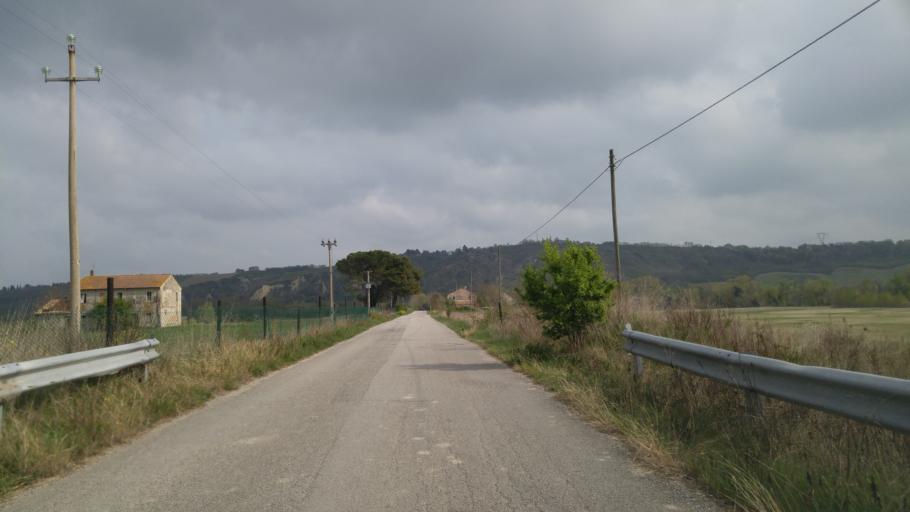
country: IT
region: The Marches
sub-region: Provincia di Pesaro e Urbino
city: Bellocchi
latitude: 43.7753
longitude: 12.9837
